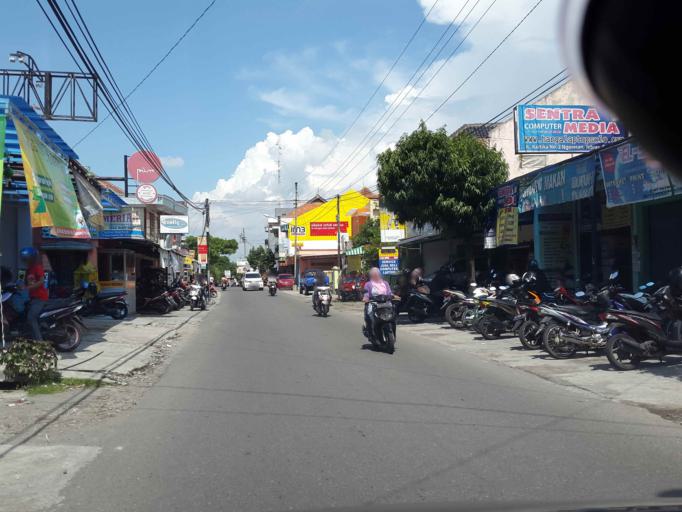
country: ID
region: Central Java
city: Surakarta
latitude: -7.5545
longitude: 110.8584
